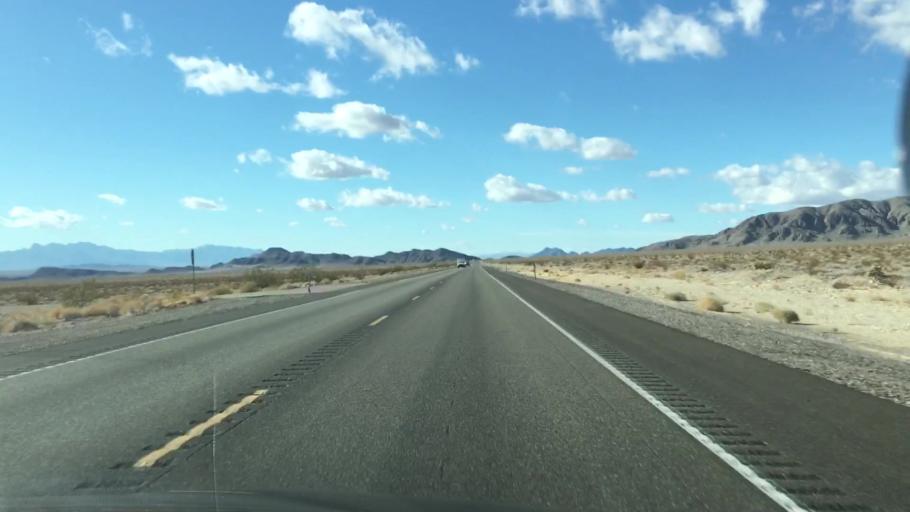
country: US
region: Nevada
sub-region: Nye County
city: Pahrump
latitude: 36.5695
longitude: -116.1569
